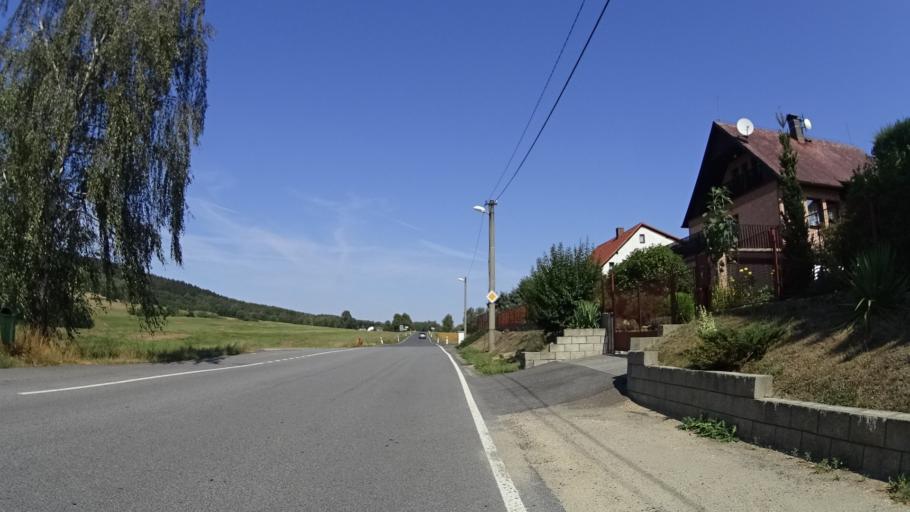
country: CZ
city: Chrastava
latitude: 50.7962
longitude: 14.9888
